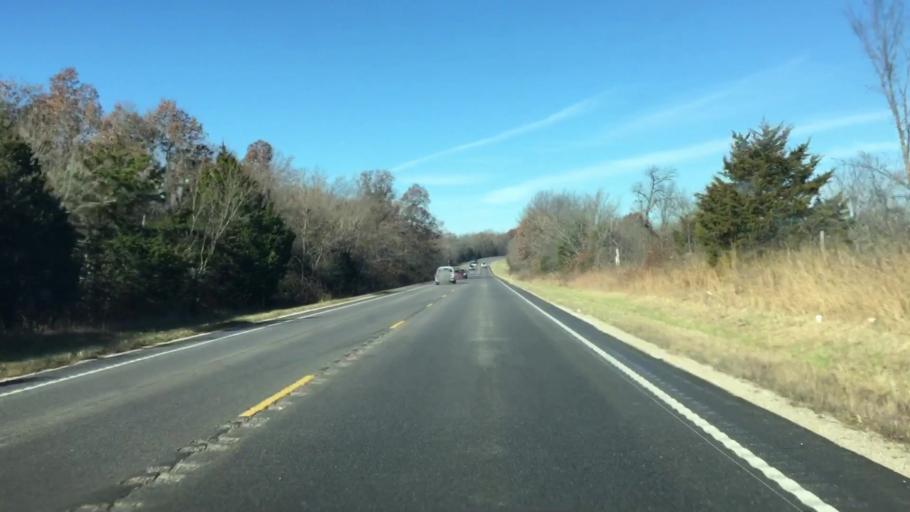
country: US
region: Missouri
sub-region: Miller County
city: Eldon
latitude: 38.3628
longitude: -92.6095
